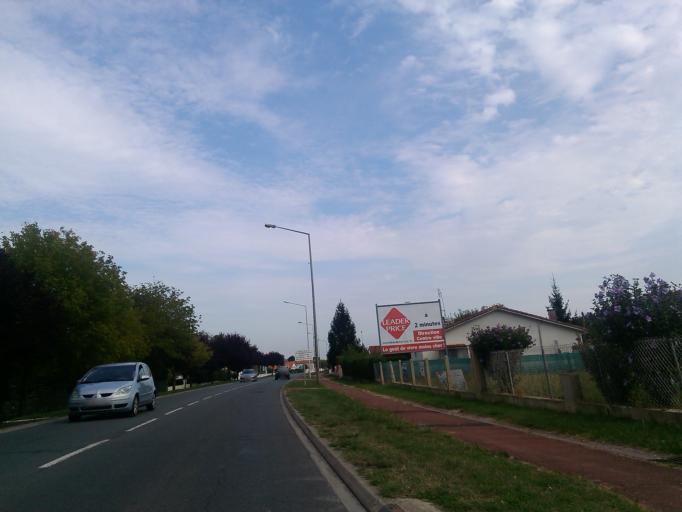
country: FR
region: Poitou-Charentes
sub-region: Departement de la Charente-Maritime
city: Saujon
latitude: 45.6755
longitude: -0.9468
